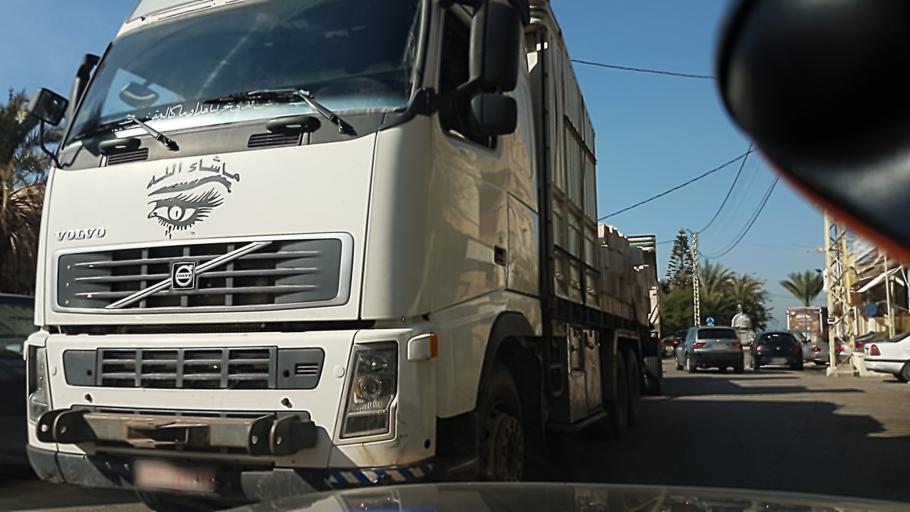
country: LB
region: Liban-Sud
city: Sidon
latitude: 33.5791
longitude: 35.3874
